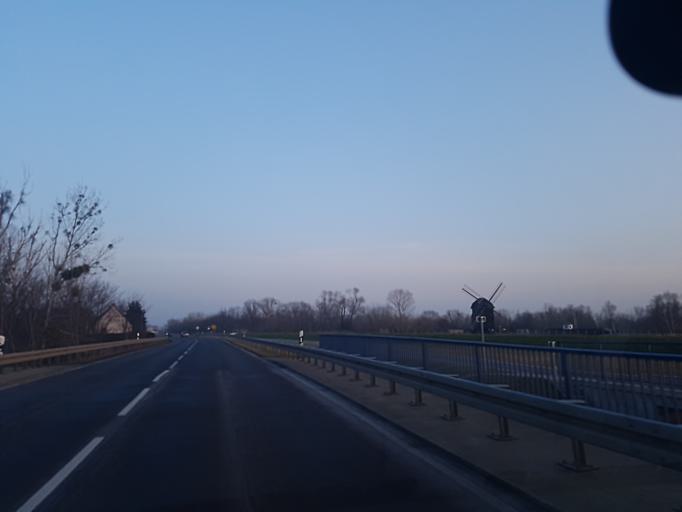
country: DE
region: Saxony-Anhalt
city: Elster
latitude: 51.8329
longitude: 12.8000
